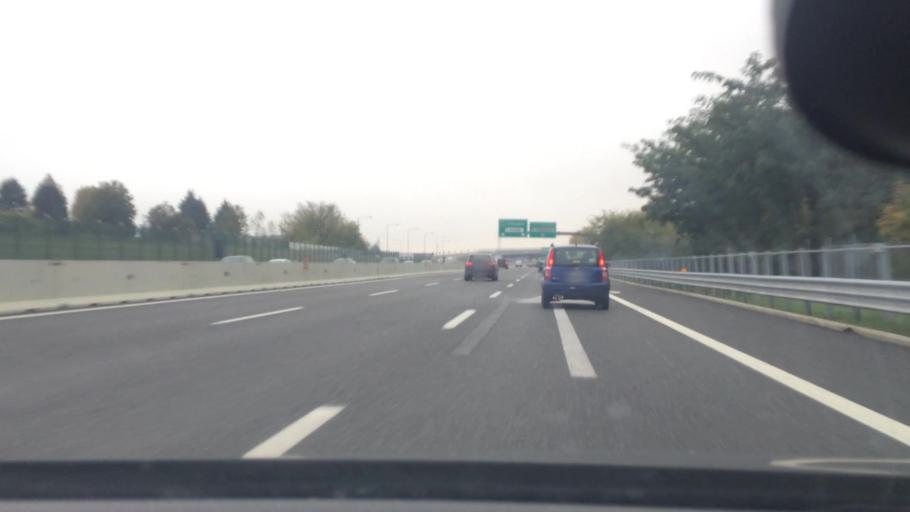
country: IT
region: Lombardy
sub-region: Provincia di Varese
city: Origgio
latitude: 45.5841
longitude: 9.0112
